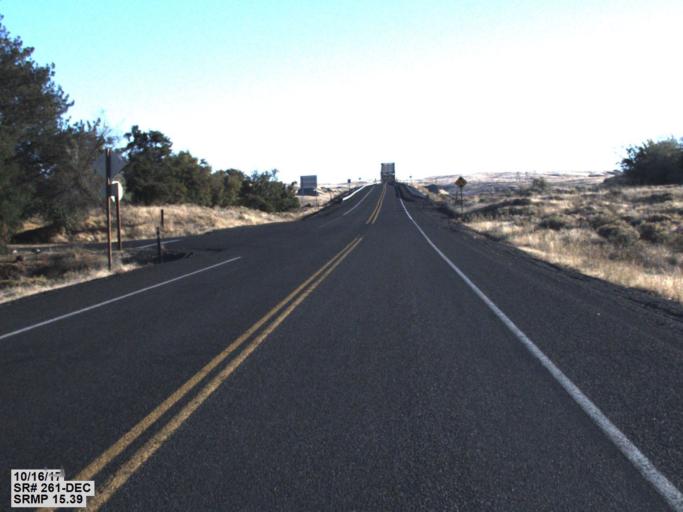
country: US
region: Washington
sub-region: Walla Walla County
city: Waitsburg
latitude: 46.5955
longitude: -118.2204
